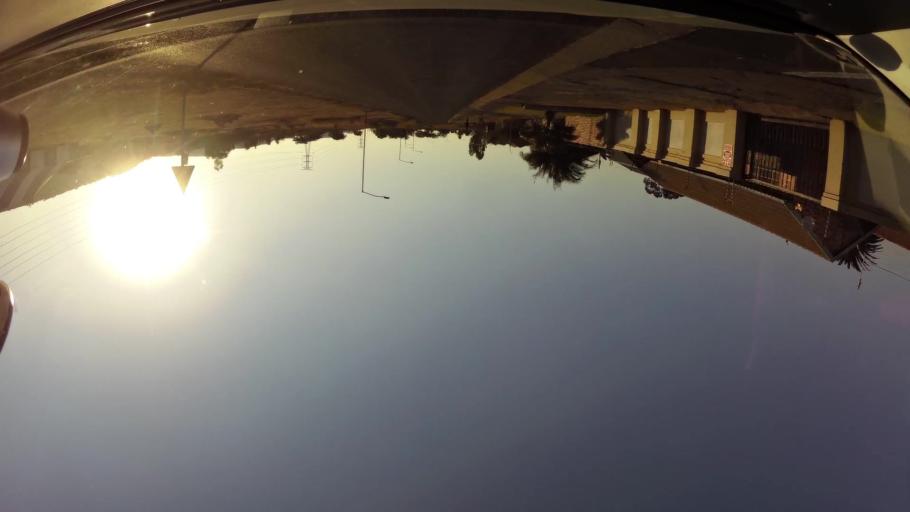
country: ZA
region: Gauteng
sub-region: City of Tshwane Metropolitan Municipality
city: Pretoria
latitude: -25.7367
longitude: 28.1155
